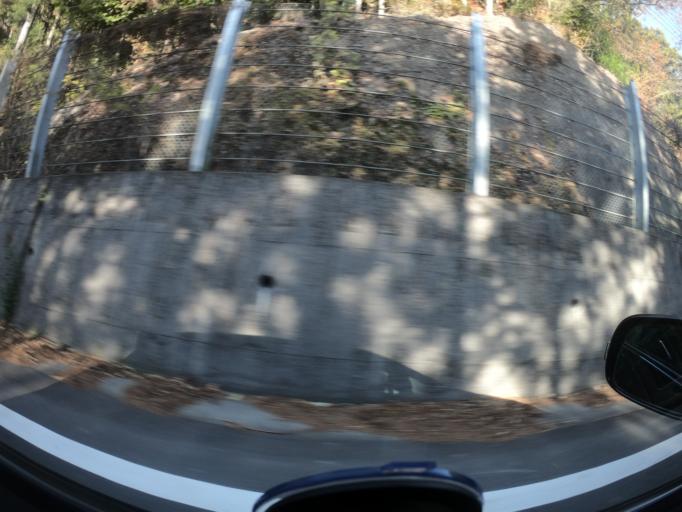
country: JP
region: Shizuoka
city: Kanaya
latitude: 34.9743
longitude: 138.0916
